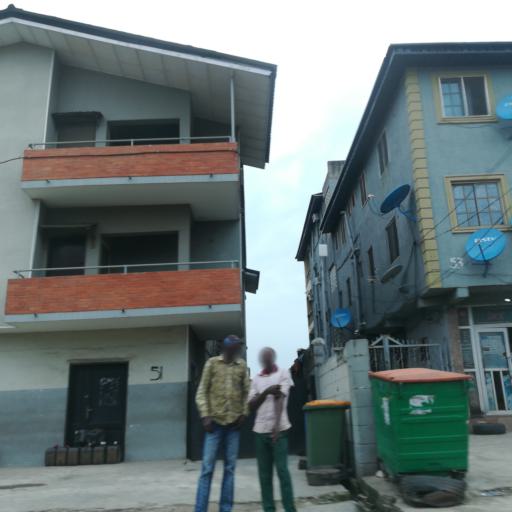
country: NG
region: Lagos
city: Makoko
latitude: 6.5014
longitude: 3.3791
